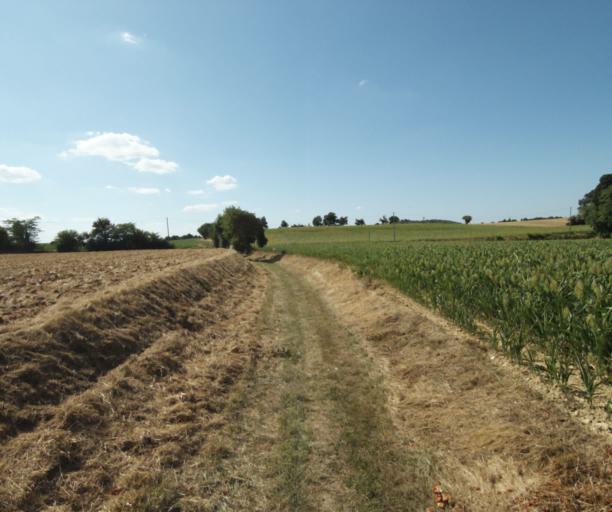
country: FR
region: Midi-Pyrenees
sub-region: Departement de la Haute-Garonne
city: Saint-Felix-Lauragais
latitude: 43.4753
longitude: 1.9137
